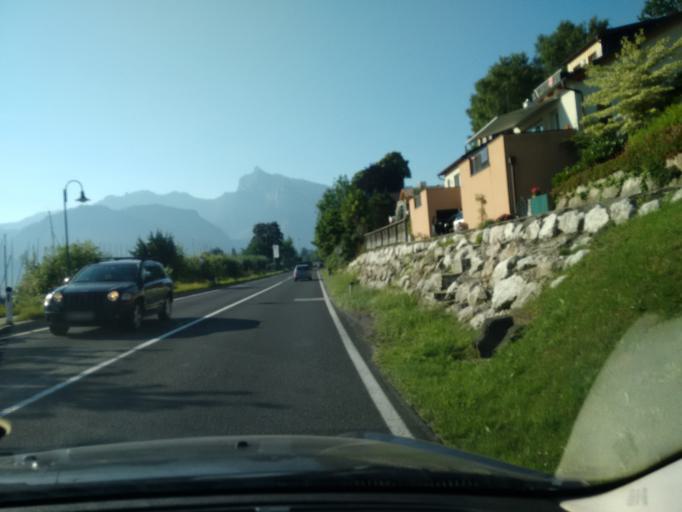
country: AT
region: Upper Austria
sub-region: Politischer Bezirk Gmunden
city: Altmunster
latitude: 47.8614
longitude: 13.7799
